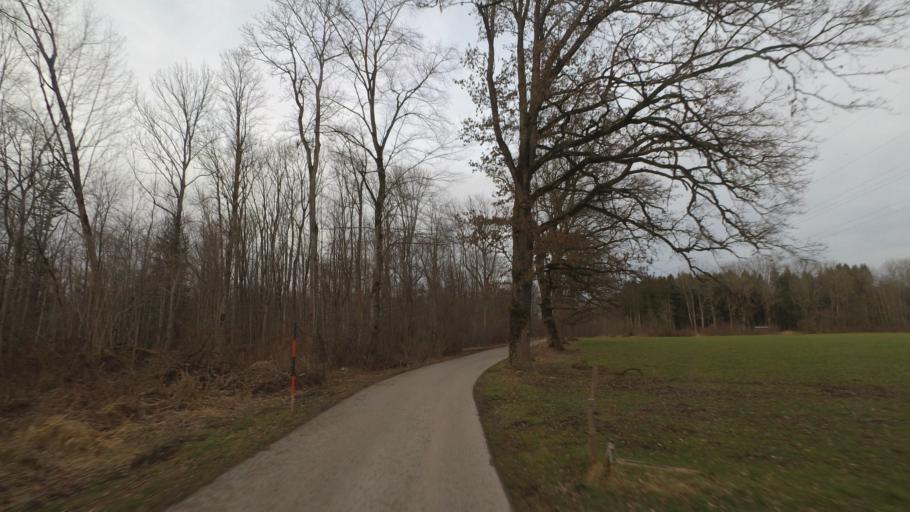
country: DE
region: Bavaria
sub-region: Upper Bavaria
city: Ubersee
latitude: 47.8157
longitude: 12.5088
